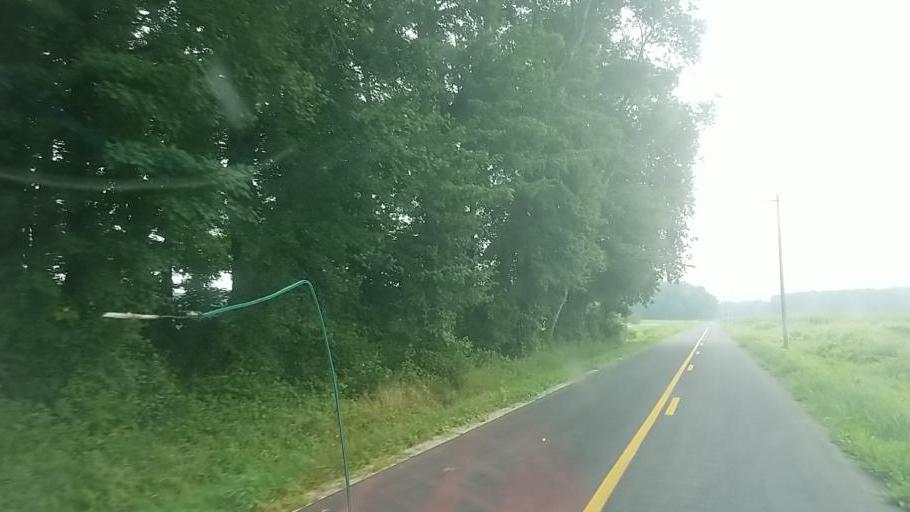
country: US
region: Delaware
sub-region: Sussex County
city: Selbyville
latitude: 38.4404
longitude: -75.2606
